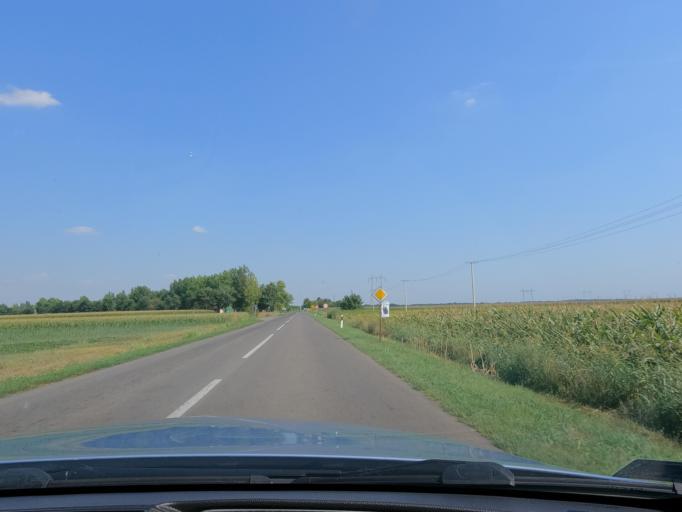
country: RS
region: Autonomna Pokrajina Vojvodina
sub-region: Severnobacki Okrug
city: Mali Igos
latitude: 45.7506
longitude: 19.7923
